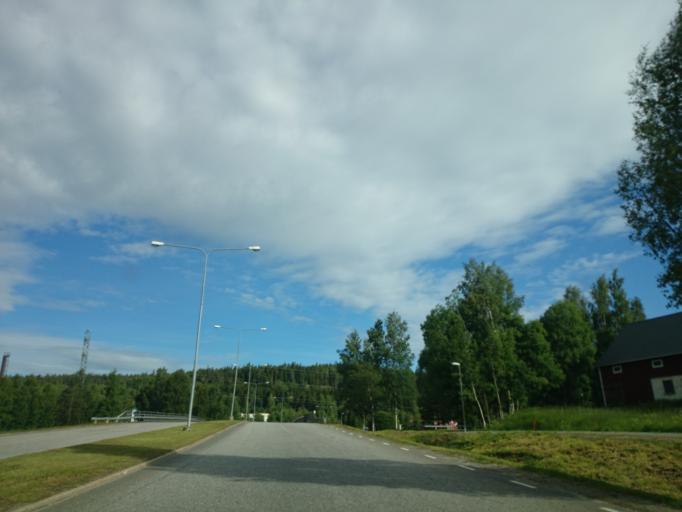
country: SE
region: Vaesternorrland
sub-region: Timra Kommun
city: Timra
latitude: 62.4795
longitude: 17.3156
